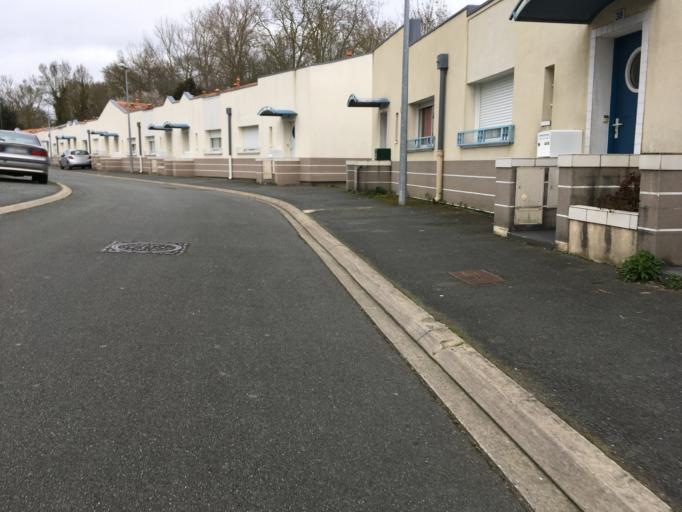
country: FR
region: Poitou-Charentes
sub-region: Departement de la Charente-Maritime
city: La Rochelle
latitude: 46.1758
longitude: -1.1451
